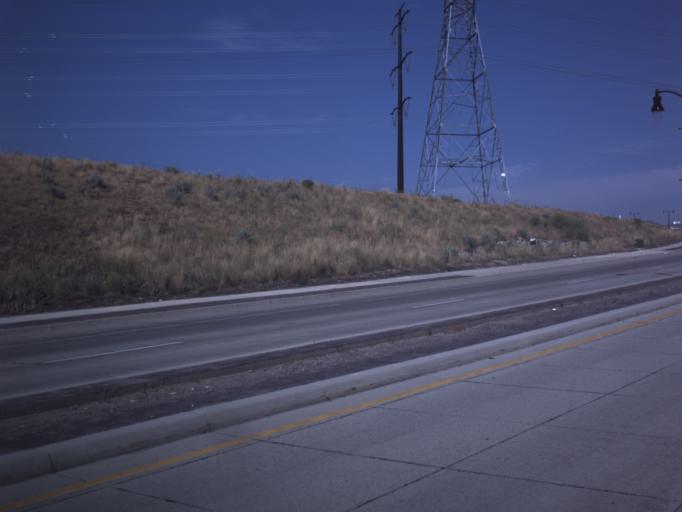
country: US
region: Utah
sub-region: Salt Lake County
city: Bluffdale
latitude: 40.4632
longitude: -111.9459
